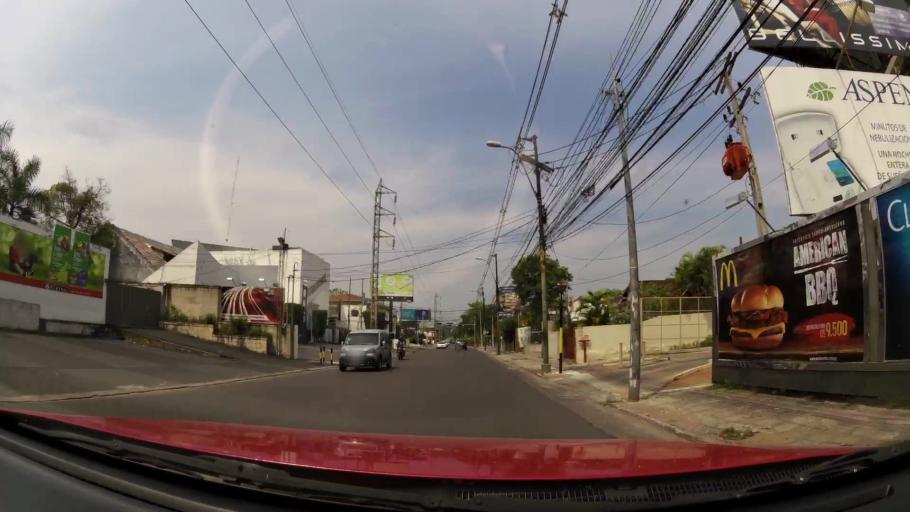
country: PY
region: Asuncion
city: Asuncion
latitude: -25.2873
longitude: -57.5960
